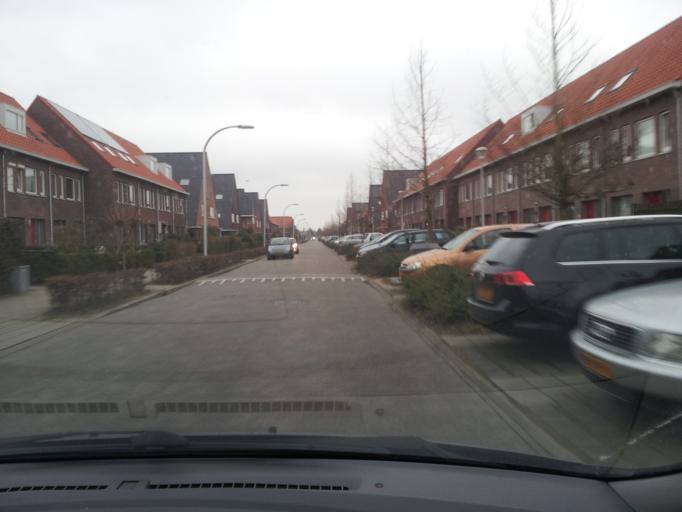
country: NL
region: South Holland
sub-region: Gemeente Den Haag
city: Ypenburg
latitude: 52.0445
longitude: 4.3787
